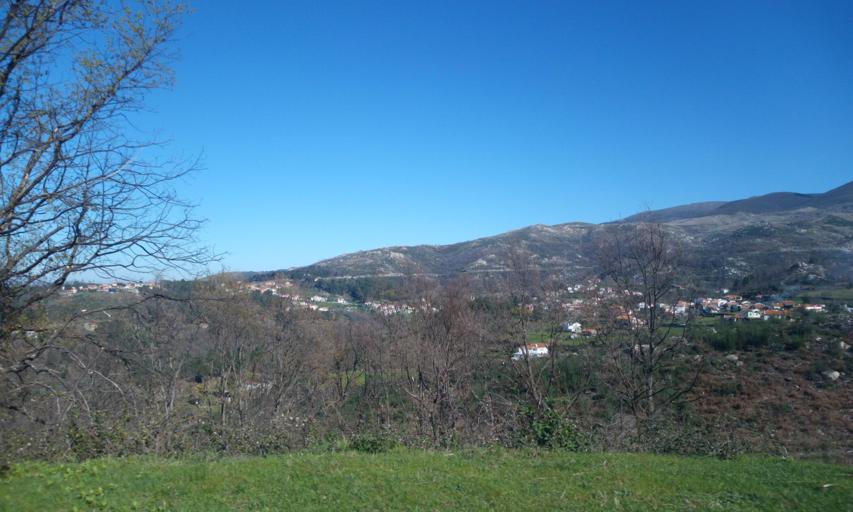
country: PT
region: Guarda
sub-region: Manteigas
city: Manteigas
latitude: 40.4649
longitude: -7.6127
